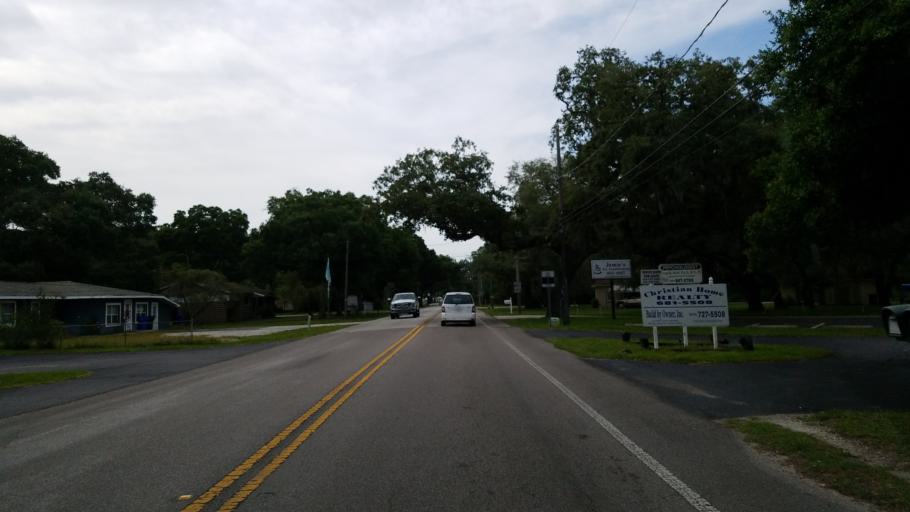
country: US
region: Florida
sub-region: Hillsborough County
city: Brandon
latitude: 27.9342
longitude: -82.2790
